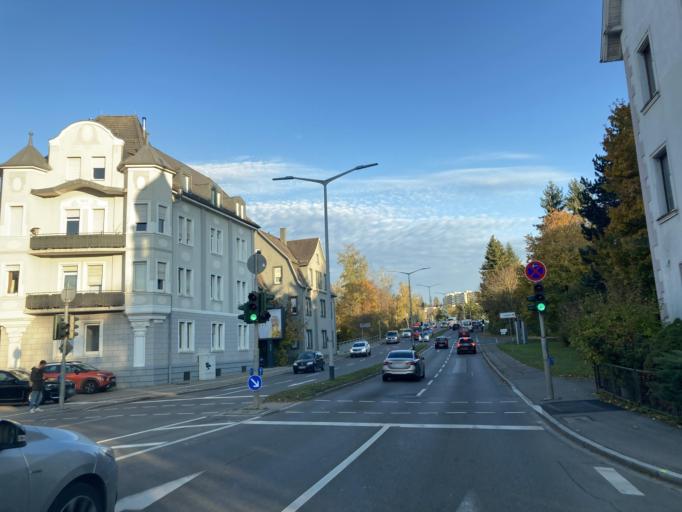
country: DE
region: Baden-Wuerttemberg
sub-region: Freiburg Region
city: Villingen-Schwenningen
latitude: 48.0550
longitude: 8.4639
